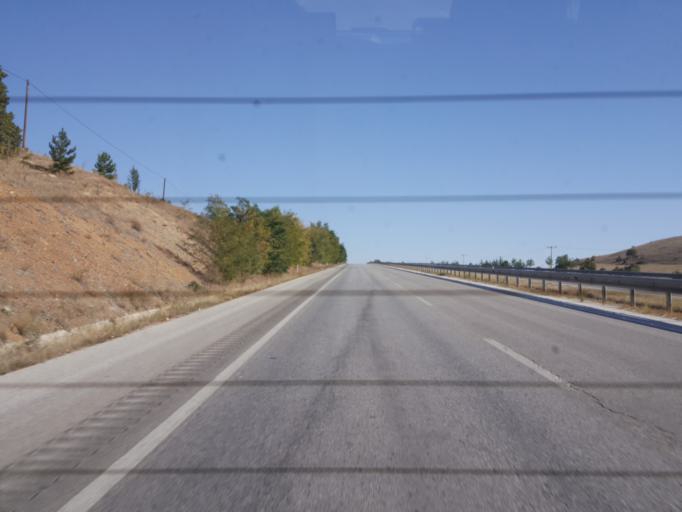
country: TR
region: Corum
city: Alaca
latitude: 40.2853
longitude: 34.6482
